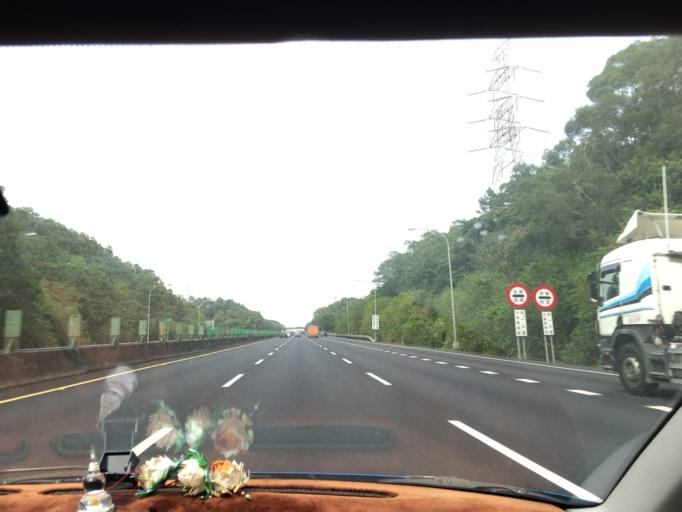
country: TW
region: Taiwan
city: Daxi
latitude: 24.8197
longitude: 121.2002
